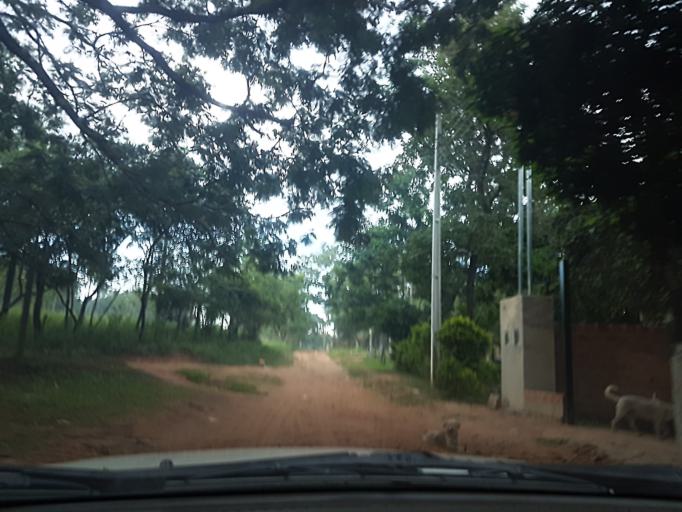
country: PY
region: Central
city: Limpio
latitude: -25.2433
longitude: -57.4611
